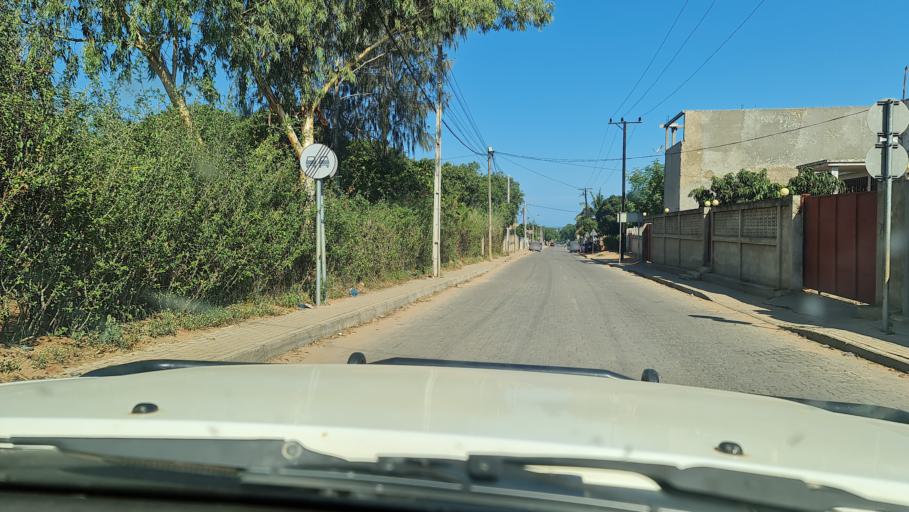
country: MZ
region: Maputo City
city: Maputo
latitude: -25.8402
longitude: 32.6366
